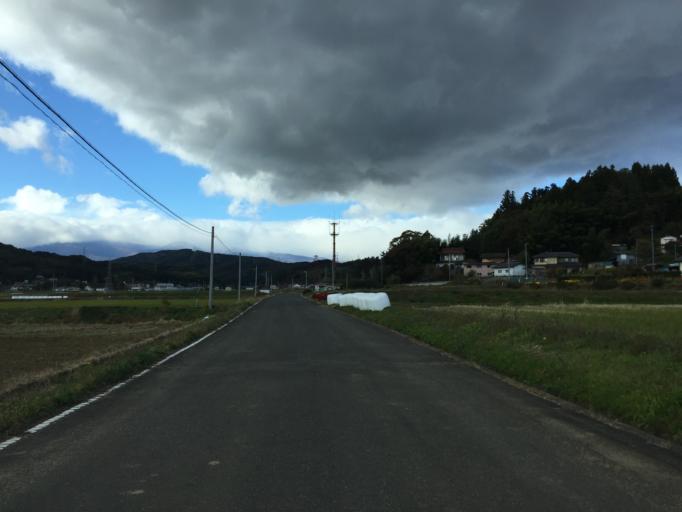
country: JP
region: Fukushima
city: Nihommatsu
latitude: 37.6624
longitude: 140.4326
